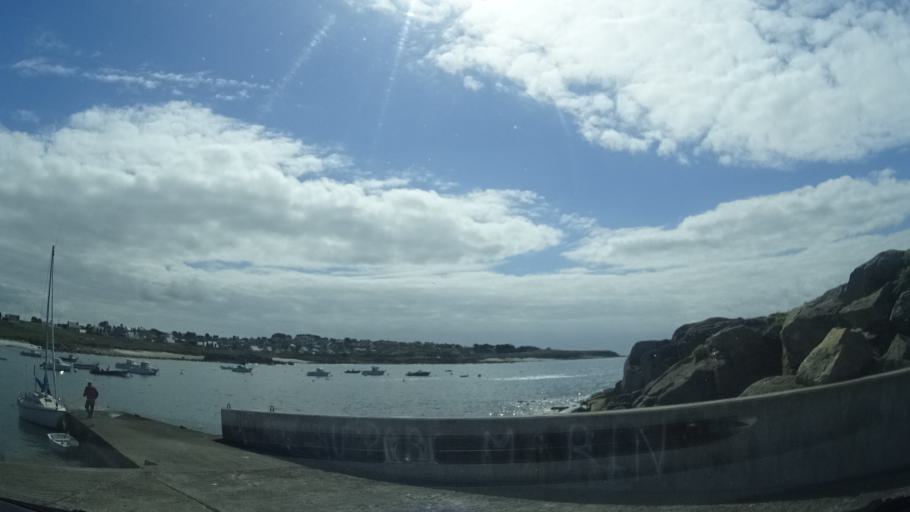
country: FR
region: Brittany
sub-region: Departement du Finistere
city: Lampaul-Plouarzel
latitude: 48.4439
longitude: -4.7820
